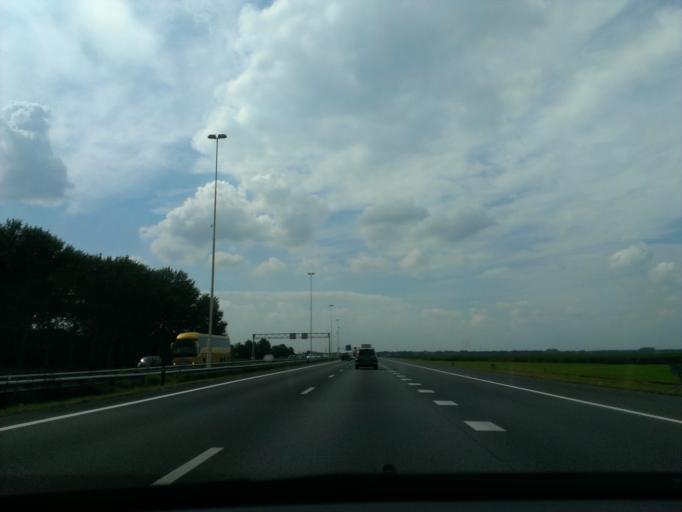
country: NL
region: Utrecht
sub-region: Gemeente Baarn
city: Baarn
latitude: 52.2216
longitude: 5.2947
